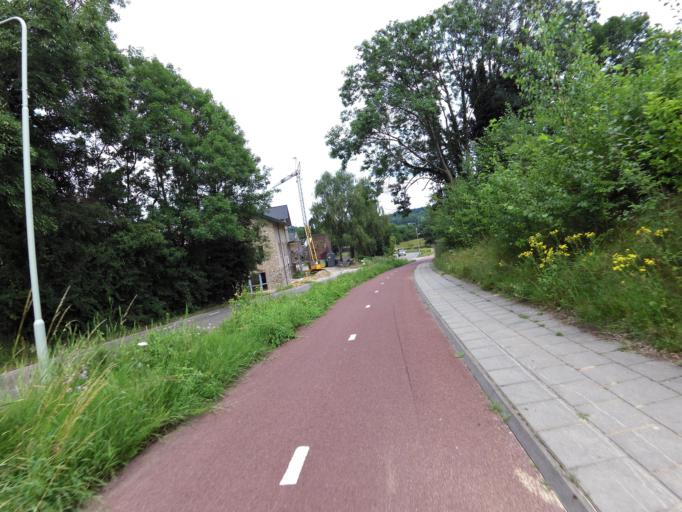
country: NL
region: Limburg
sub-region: Gemeente Simpelveld
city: Simpelveld
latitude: 50.7956
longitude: 5.9700
